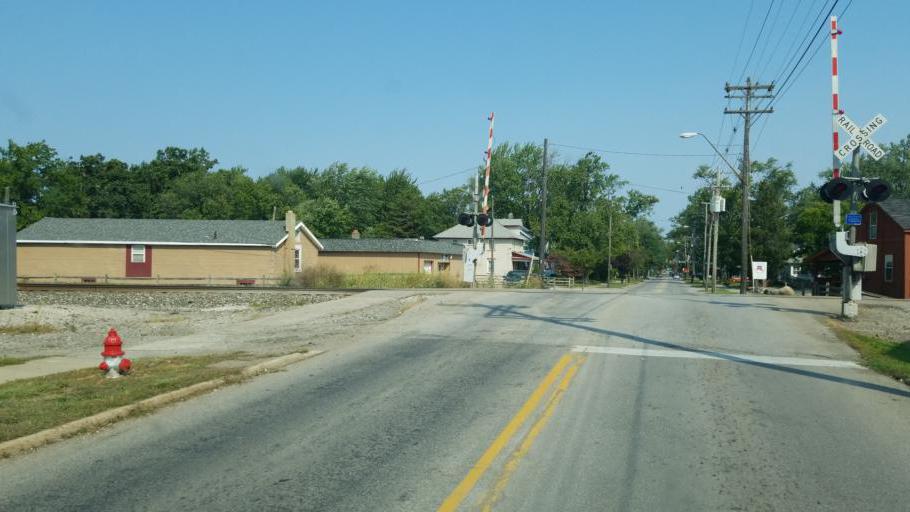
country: US
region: Ohio
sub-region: Lake County
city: Painesville
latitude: 41.7142
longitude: -81.2407
